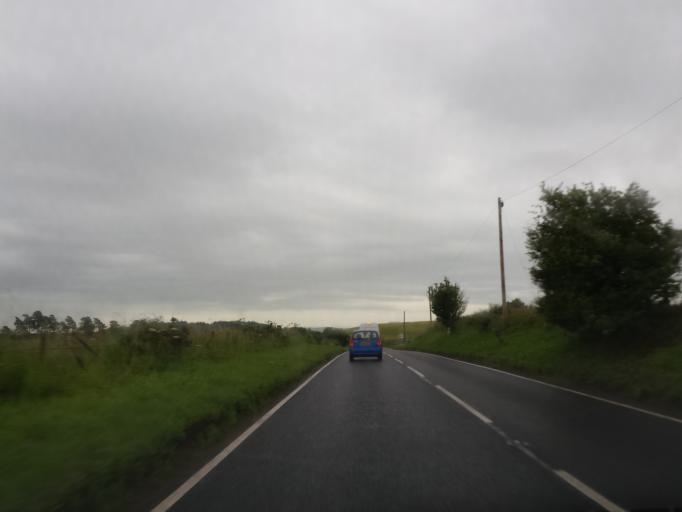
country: GB
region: Scotland
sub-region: Fife
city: Balmullo
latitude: 56.4001
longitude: -2.9115
